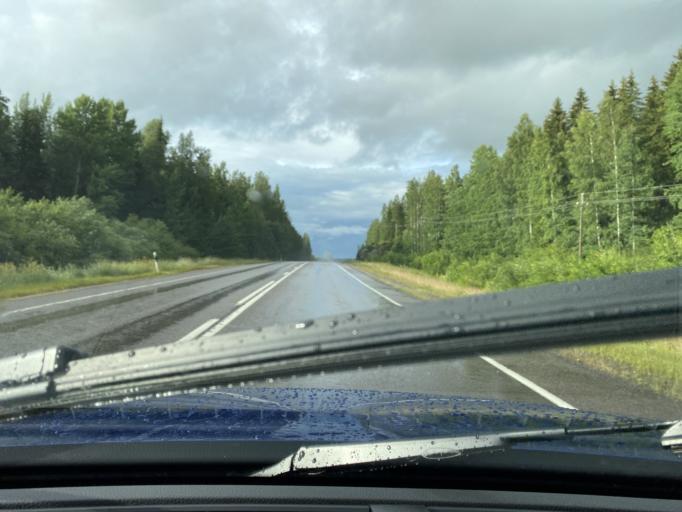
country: FI
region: Uusimaa
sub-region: Helsinki
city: Nurmijaervi
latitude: 60.4625
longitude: 24.8344
